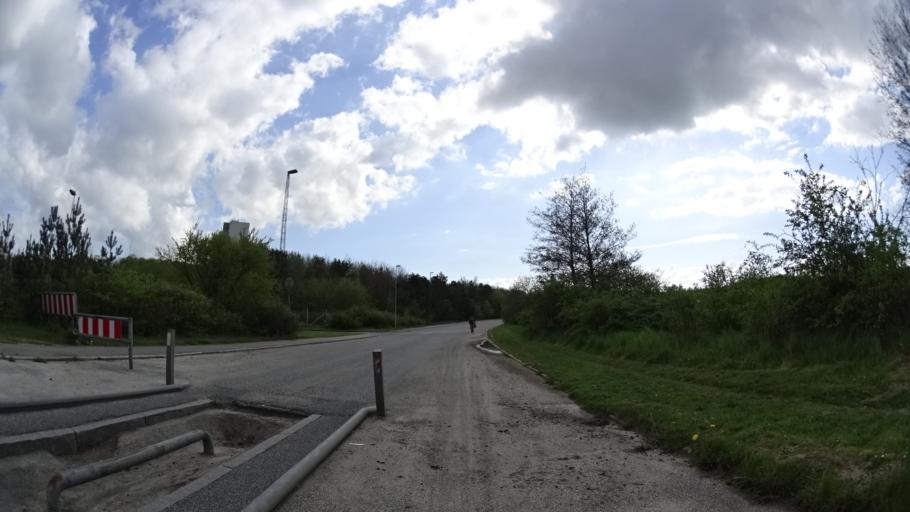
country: DK
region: Central Jutland
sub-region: Arhus Kommune
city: Stavtrup
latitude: 56.1273
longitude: 10.1394
